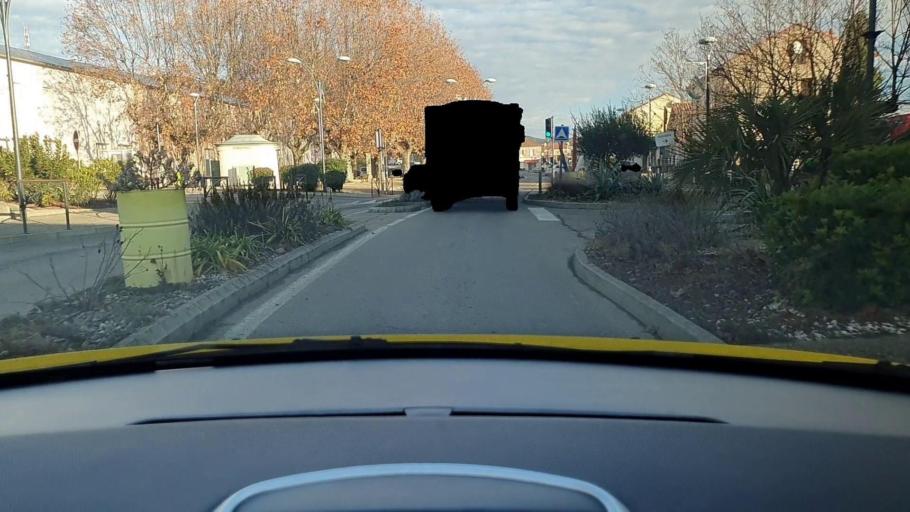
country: FR
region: Languedoc-Roussillon
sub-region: Departement du Gard
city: Saint-Martin-de-Valgalgues
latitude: 44.1609
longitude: 4.0832
